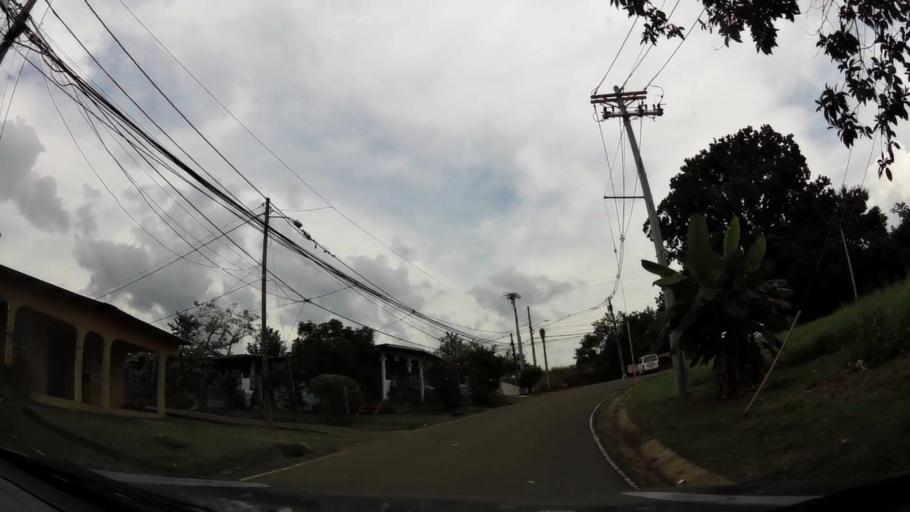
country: PA
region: Panama
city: Cabra Numero Uno
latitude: 9.1190
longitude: -79.3569
